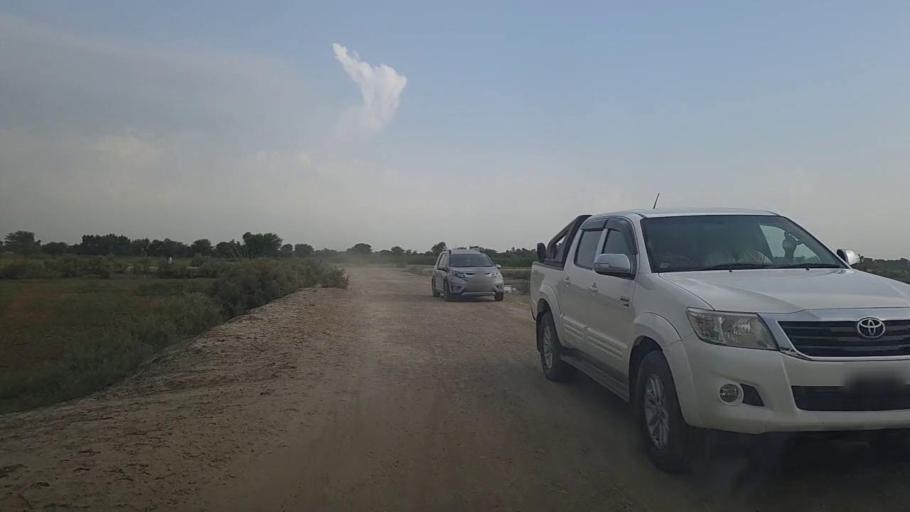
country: PK
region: Sindh
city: Mirpur Mathelo
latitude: 27.9108
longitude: 69.5115
